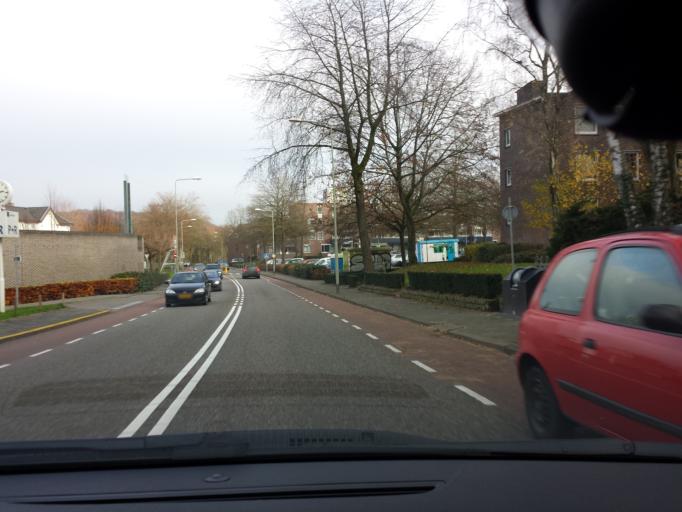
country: NL
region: Limburg
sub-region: Gemeente Heerlen
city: Heerlen
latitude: 50.8958
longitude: 6.0184
